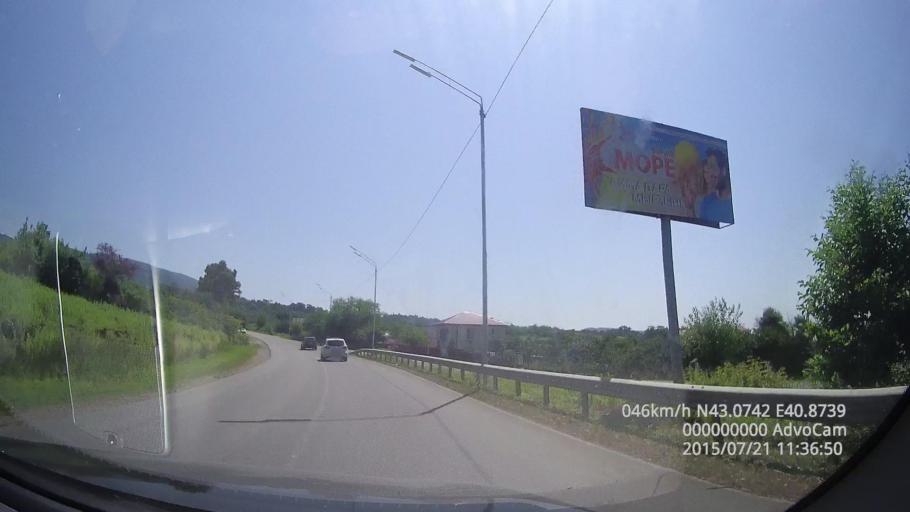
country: GE
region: Abkhazia
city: Stantsiya Novyy Afon
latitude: 43.0741
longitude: 40.8742
